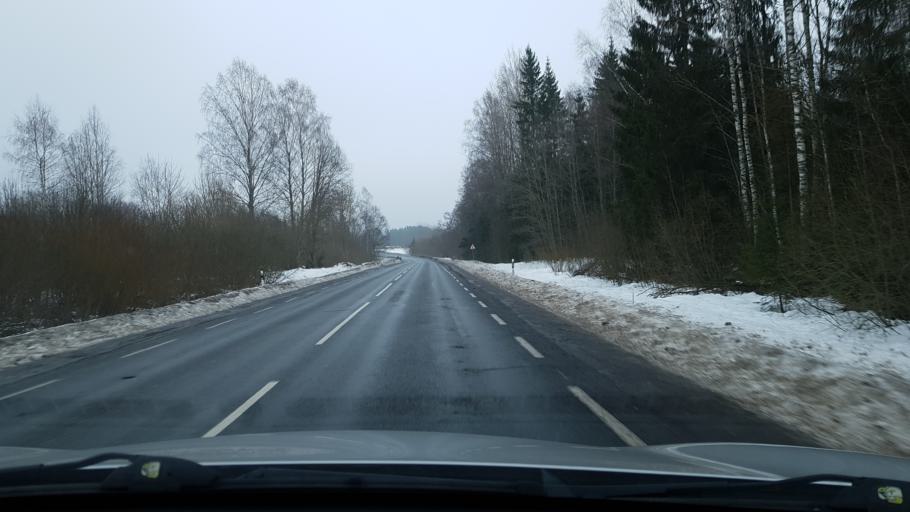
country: EE
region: Viljandimaa
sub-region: Viiratsi vald
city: Viiratsi
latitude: 58.2518
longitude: 25.7378
